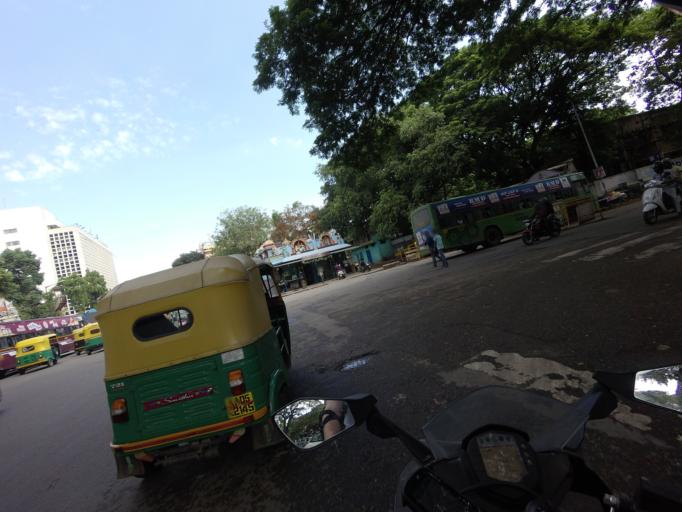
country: IN
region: Karnataka
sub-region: Bangalore Urban
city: Bangalore
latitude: 12.9728
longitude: 77.5817
